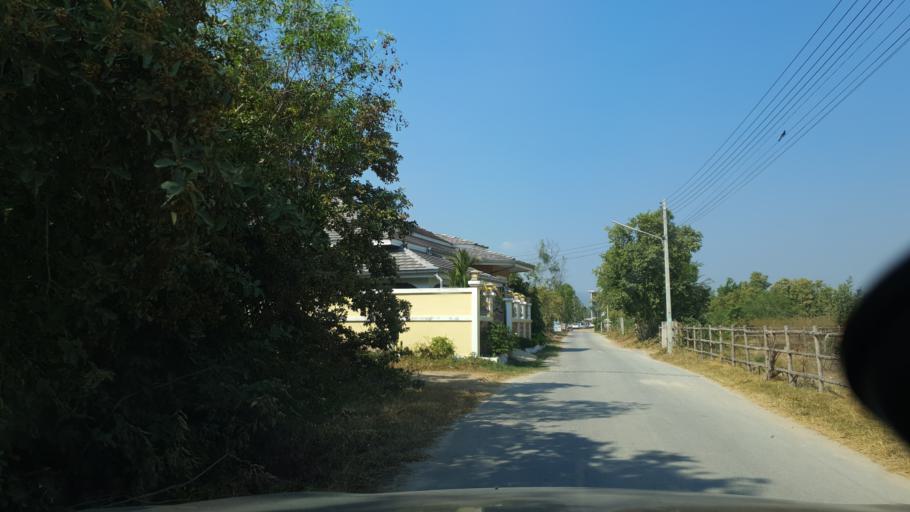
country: TH
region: Phetchaburi
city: Cha-am
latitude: 12.7835
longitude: 99.9767
